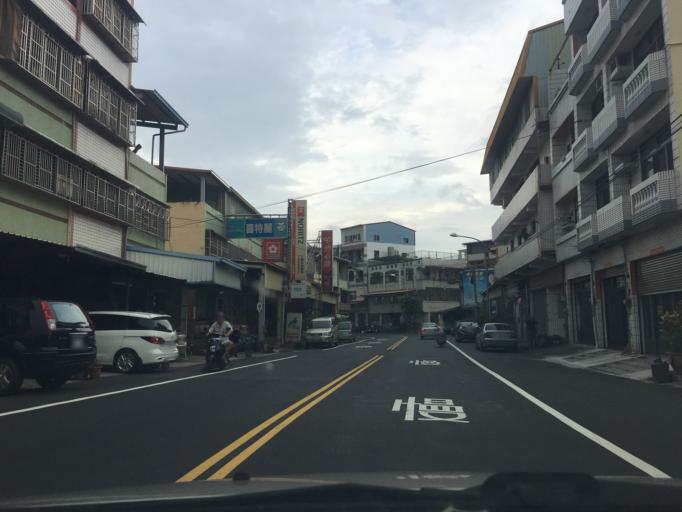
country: TW
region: Taiwan
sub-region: Changhua
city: Chang-hua
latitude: 24.0728
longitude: 120.5590
